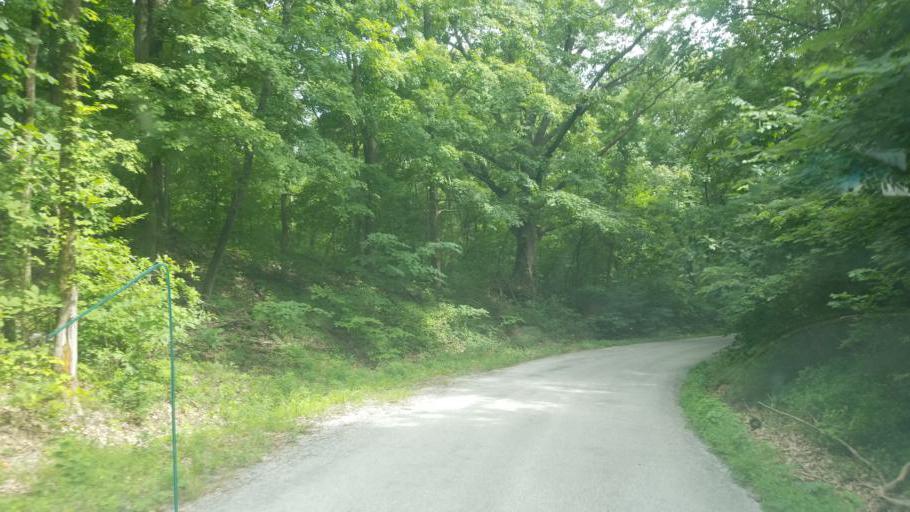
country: US
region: Illinois
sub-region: Jackson County
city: Murphysboro
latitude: 37.6235
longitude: -89.3688
